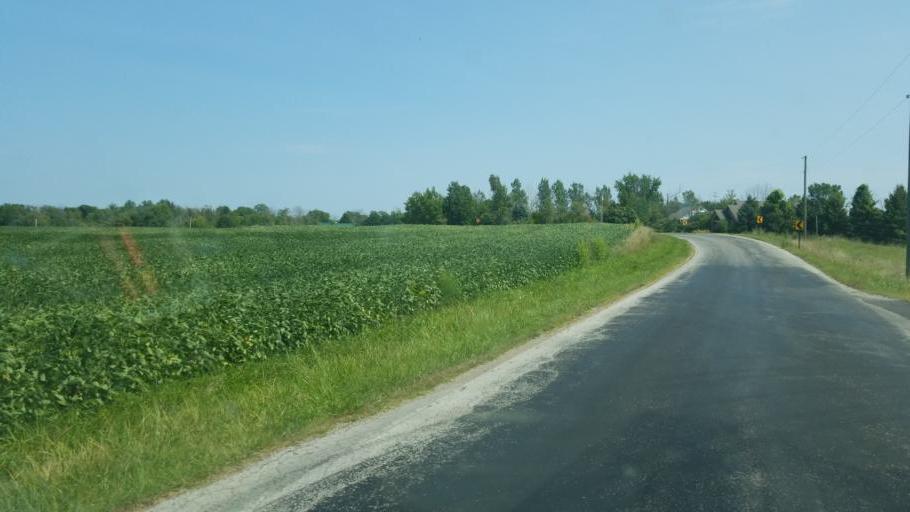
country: US
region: Ohio
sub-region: Richland County
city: Shelby
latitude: 40.8064
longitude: -82.6613
